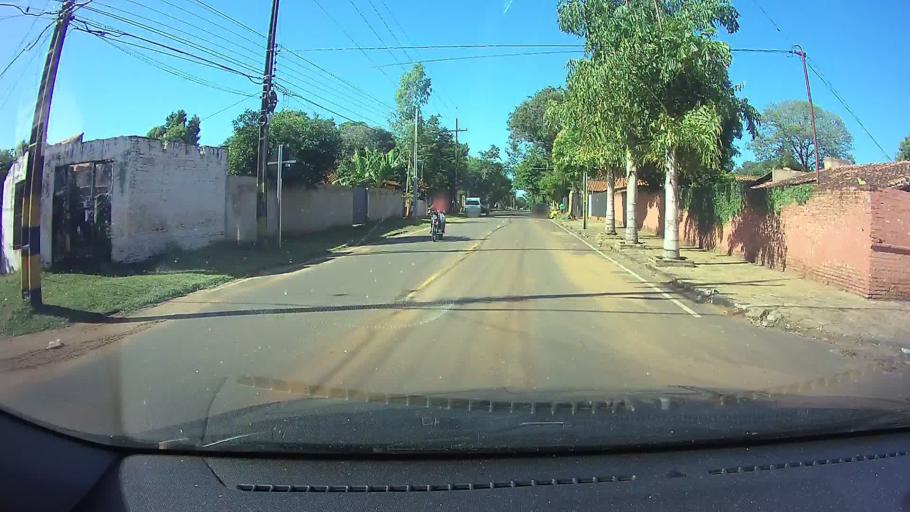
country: PY
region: Central
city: San Lorenzo
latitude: -25.2741
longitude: -57.5040
